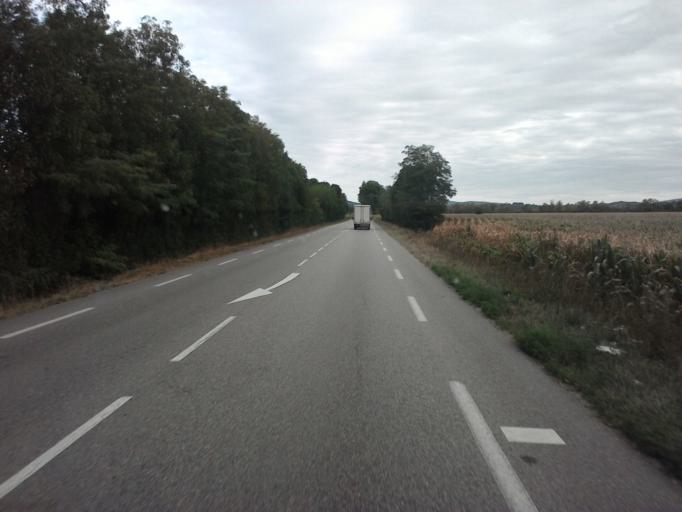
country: FR
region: Rhone-Alpes
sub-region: Departement de l'Ain
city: Ambronay
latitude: 46.0189
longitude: 5.3397
